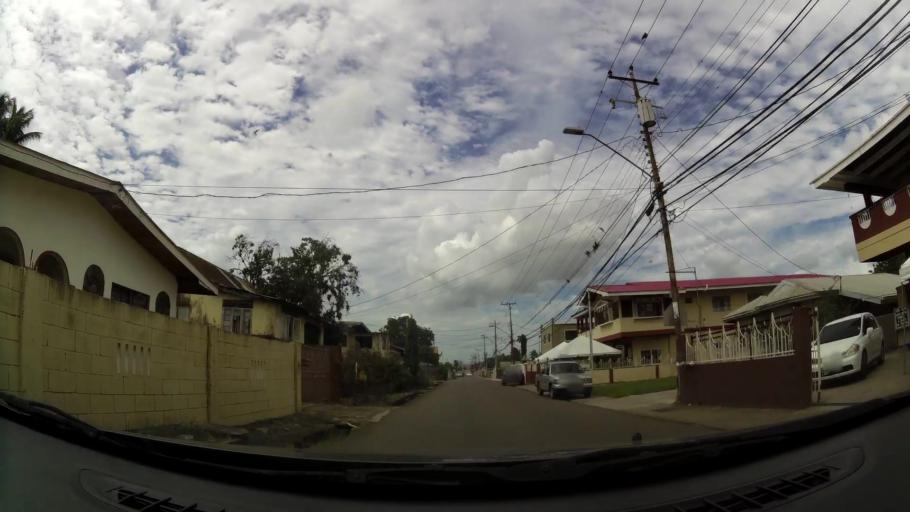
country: TT
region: Couva-Tabaquite-Talparo
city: Couva
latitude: 10.4036
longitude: -61.4678
